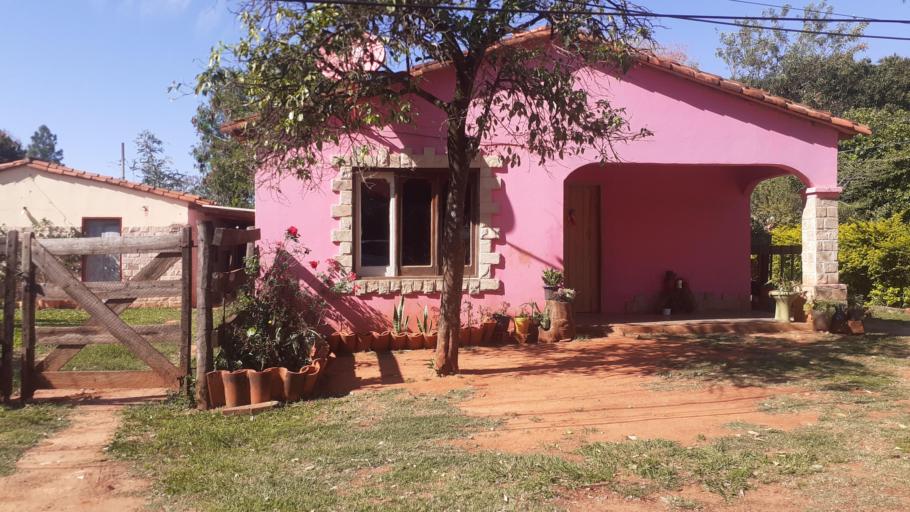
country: PY
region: Misiones
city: San Juan Bautista
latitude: -26.6655
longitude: -57.1292
